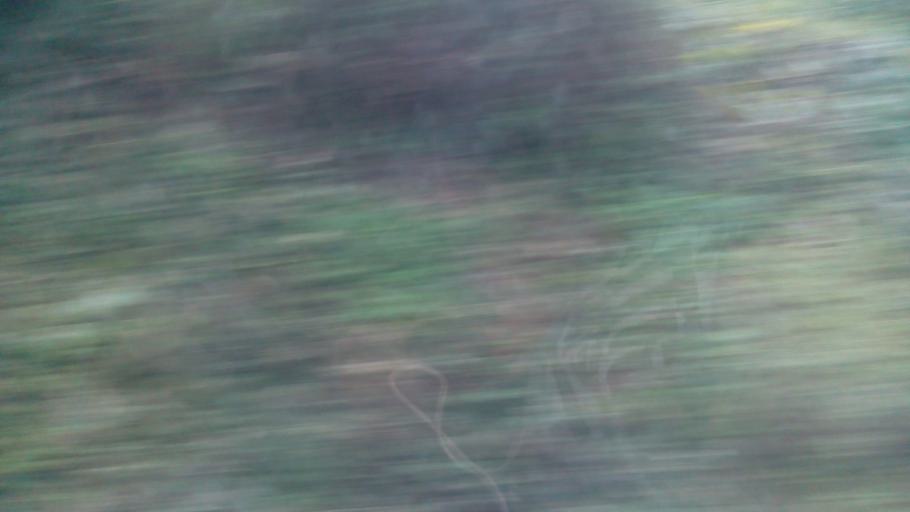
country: TW
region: Taiwan
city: Daxi
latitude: 24.4680
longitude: 121.4128
